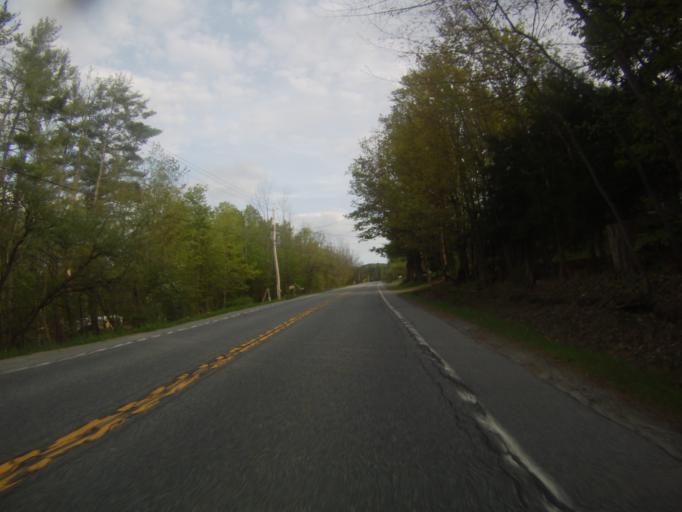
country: US
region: New York
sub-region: Warren County
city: Warrensburg
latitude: 43.6579
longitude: -73.9517
